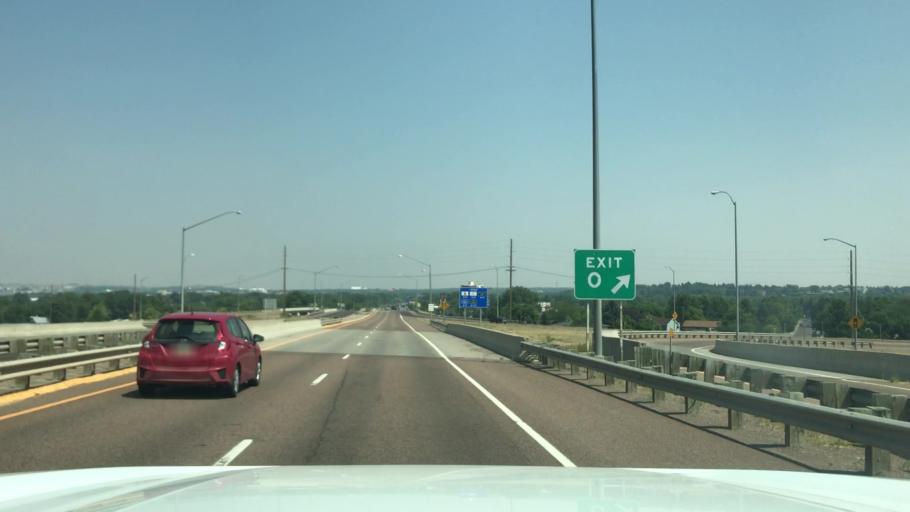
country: US
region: Montana
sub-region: Cascade County
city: Great Falls
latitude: 47.4866
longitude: -111.3388
